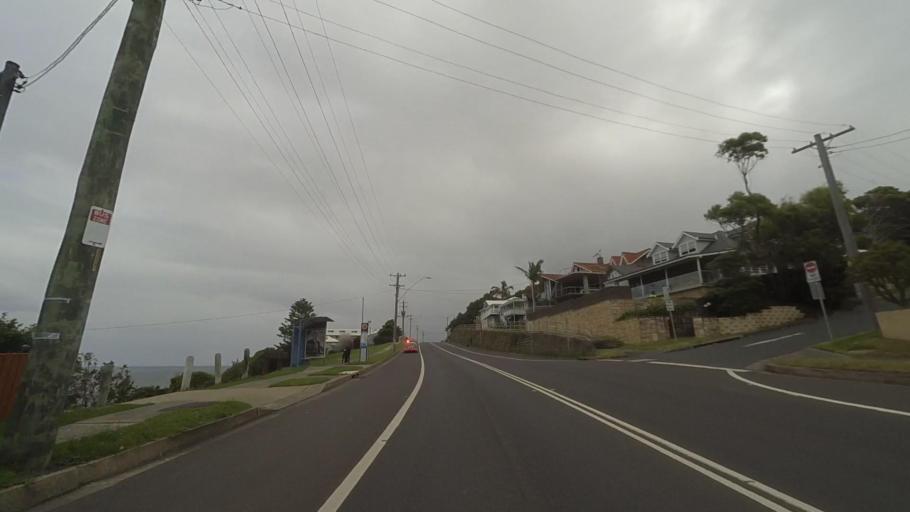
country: AU
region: New South Wales
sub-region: Wollongong
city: Bulli
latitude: -34.3089
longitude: 150.9329
